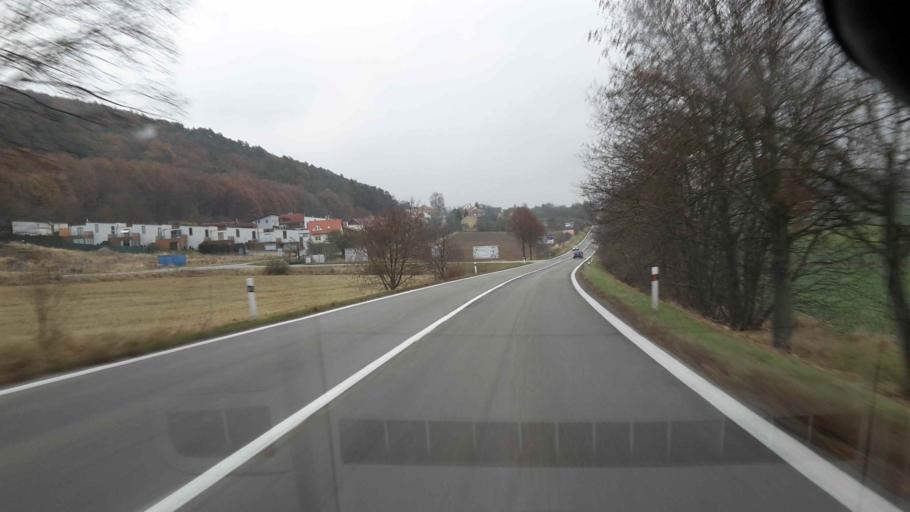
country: CZ
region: South Moravian
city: Lipuvka
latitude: 49.3355
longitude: 16.5625
